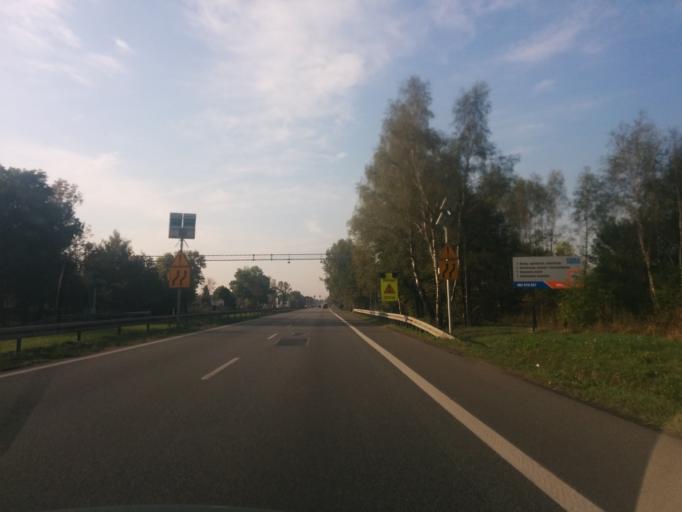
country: PL
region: Masovian Voivodeship
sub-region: Powiat piaseczynski
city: Tarczyn
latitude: 52.0420
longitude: 20.8623
